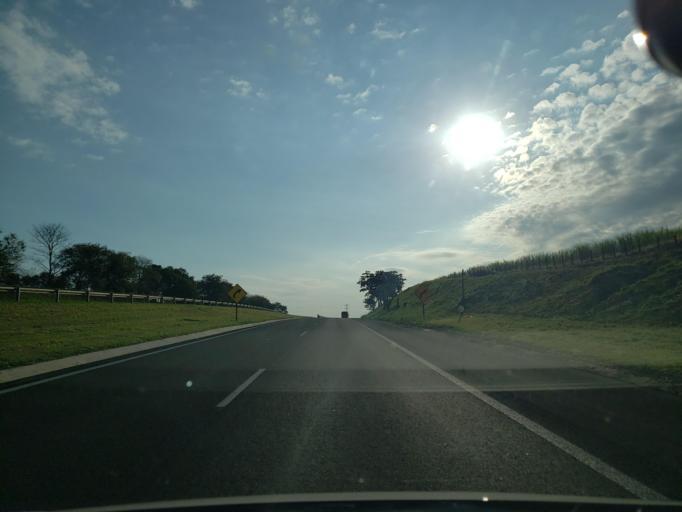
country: BR
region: Sao Paulo
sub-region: Valparaiso
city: Valparaiso
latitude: -21.2052
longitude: -50.8868
